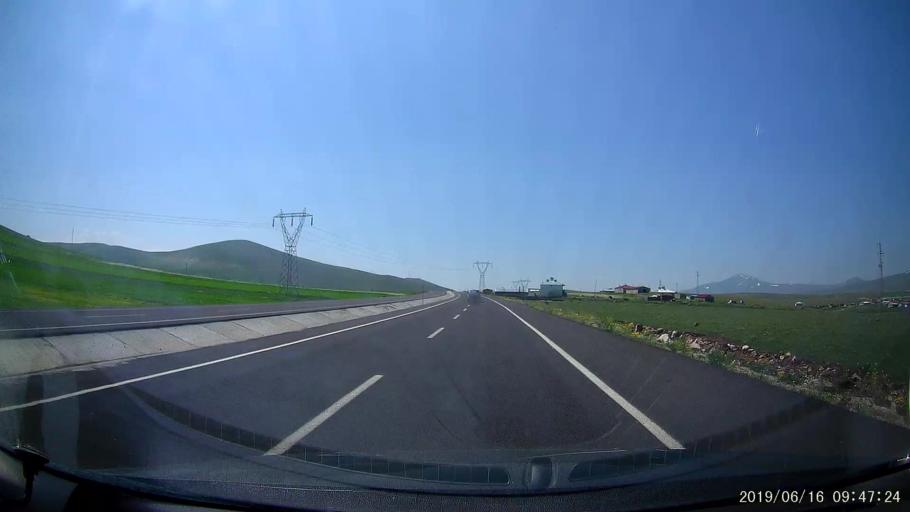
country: TR
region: Kars
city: Digor
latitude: 40.4483
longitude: 43.3435
